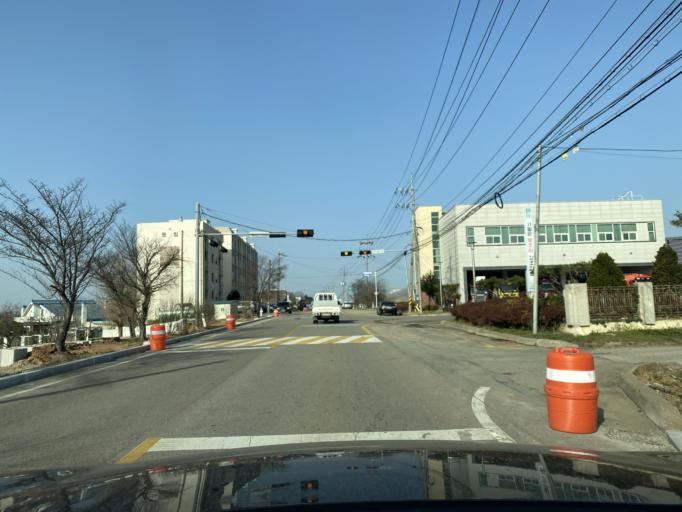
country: KR
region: Chungcheongnam-do
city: Yesan
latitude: 36.6860
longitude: 126.8020
